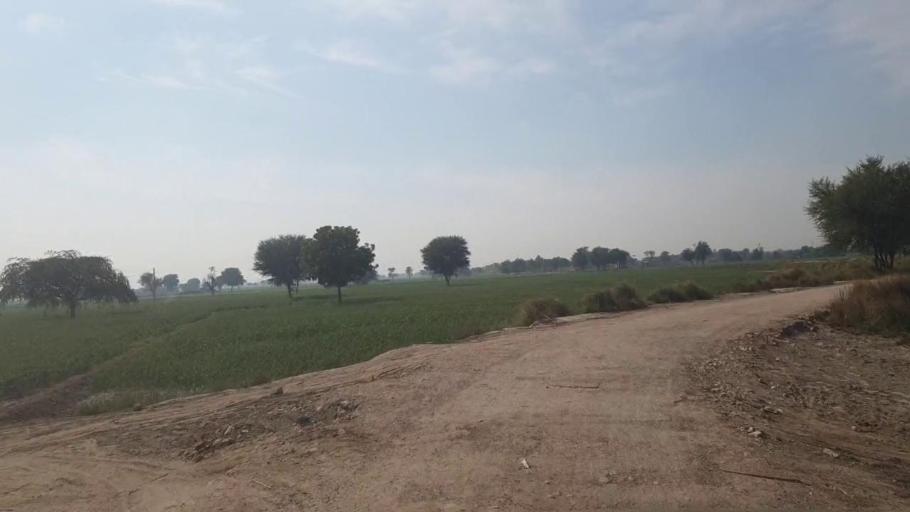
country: PK
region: Sindh
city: Nawabshah
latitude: 26.1633
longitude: 68.4968
